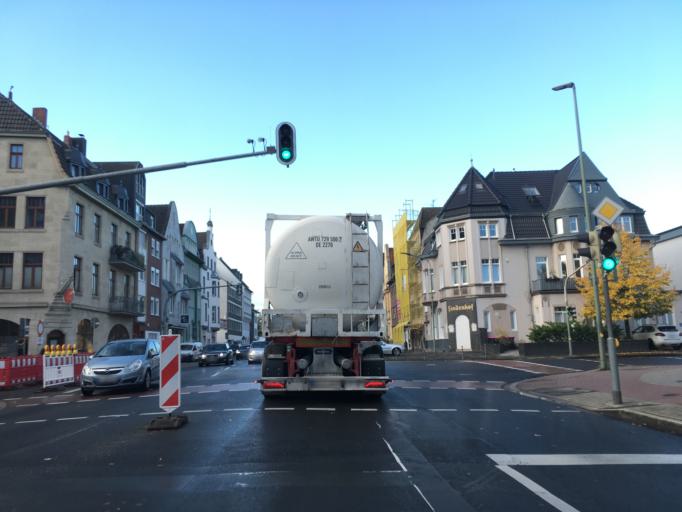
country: DE
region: North Rhine-Westphalia
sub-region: Regierungsbezirk Dusseldorf
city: Neuss
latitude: 51.1900
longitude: 6.6879
